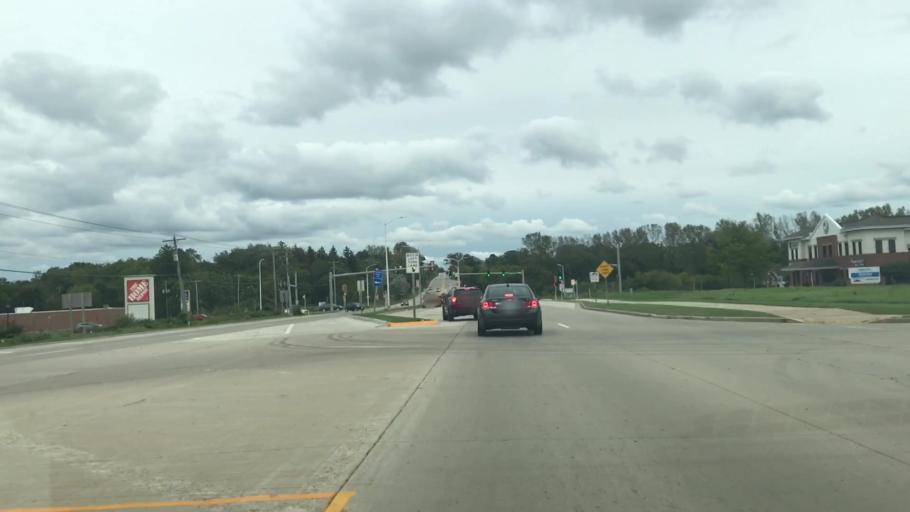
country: US
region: Wisconsin
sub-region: Waukesha County
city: Mukwonago
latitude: 42.8497
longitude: -88.3199
